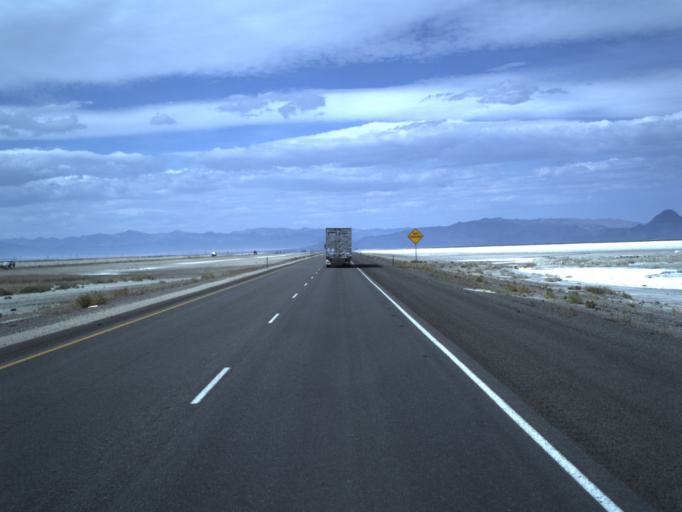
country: US
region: Utah
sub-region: Tooele County
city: Wendover
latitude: 40.7381
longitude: -113.7876
